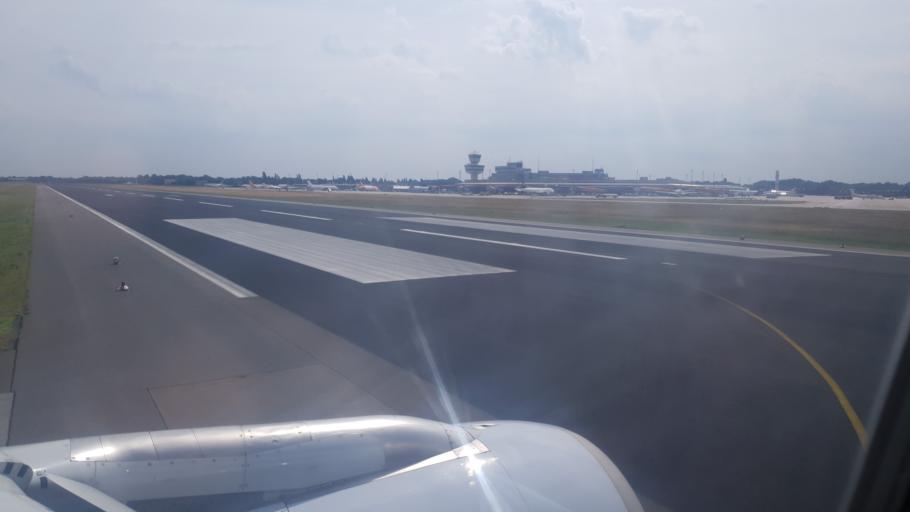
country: DE
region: Berlin
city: Tegel
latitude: 52.5576
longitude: 13.2815
